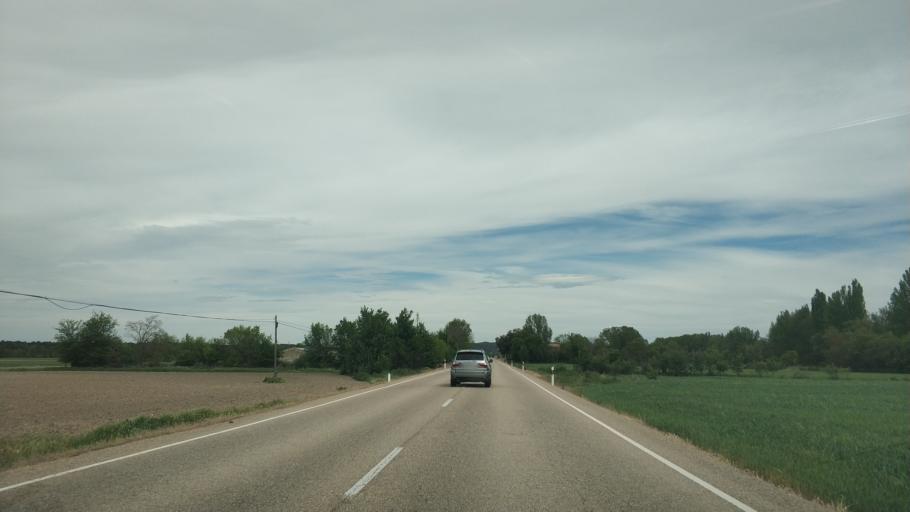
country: ES
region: Castille and Leon
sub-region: Provincia de Soria
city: Bayubas de Abajo
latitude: 41.4995
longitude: -2.8822
